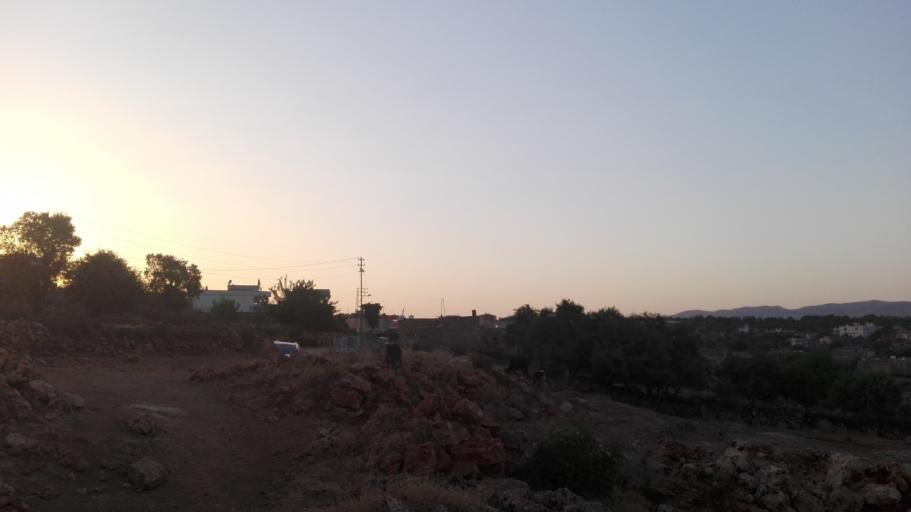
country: TR
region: Mardin
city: Kilavuz
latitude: 37.4763
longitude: 41.7863
